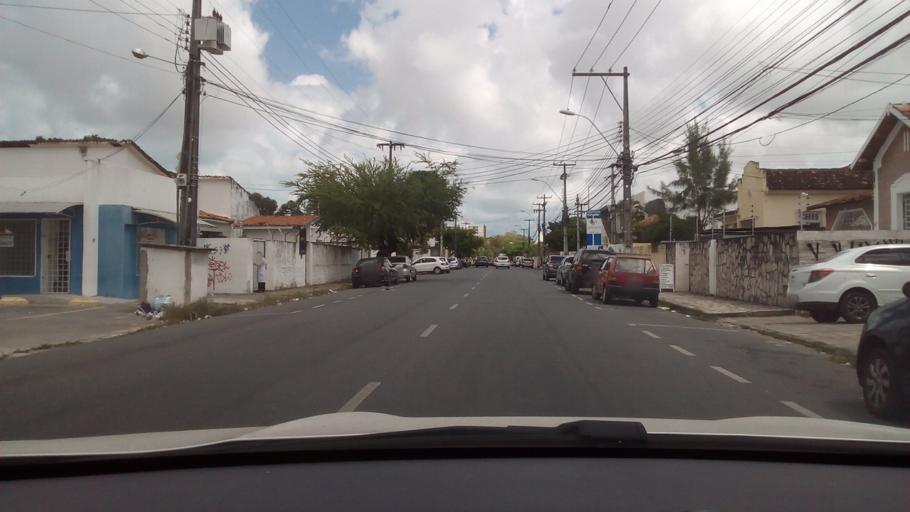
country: BR
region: Paraiba
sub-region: Joao Pessoa
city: Joao Pessoa
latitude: -7.1207
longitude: -34.8707
